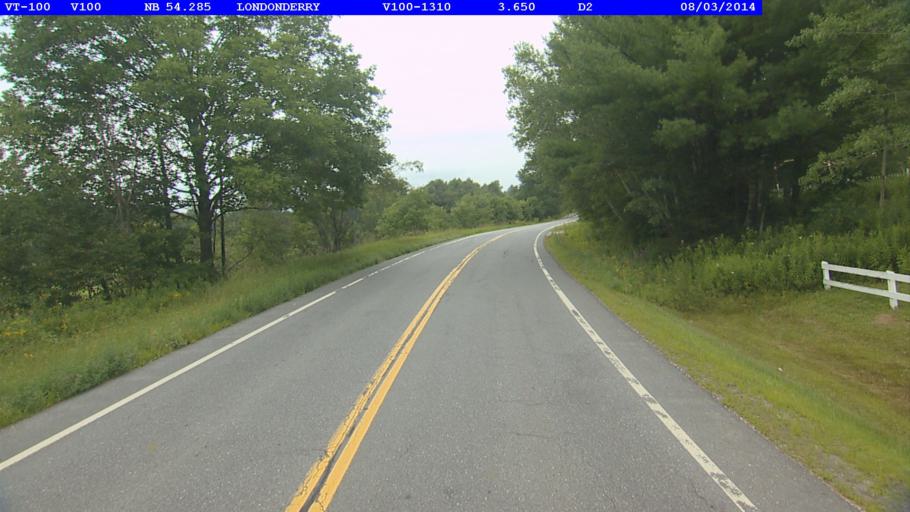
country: US
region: Vermont
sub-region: Windsor County
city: Chester
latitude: 43.2004
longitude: -72.8215
